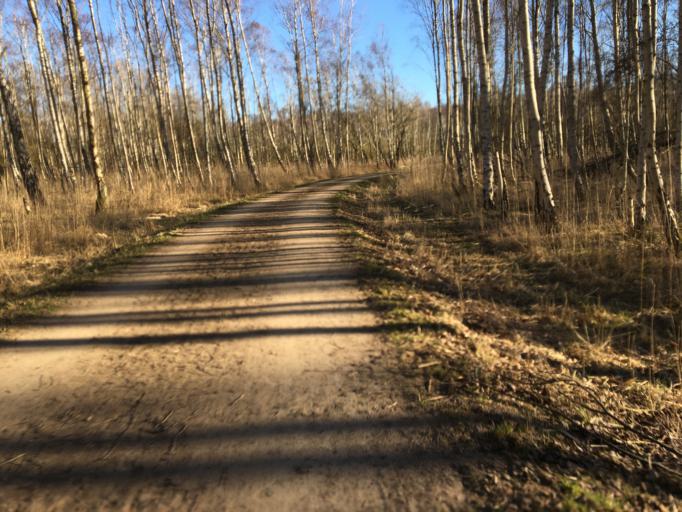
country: DK
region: Capital Region
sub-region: Tarnby Kommune
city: Tarnby
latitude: 55.5898
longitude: 12.5567
